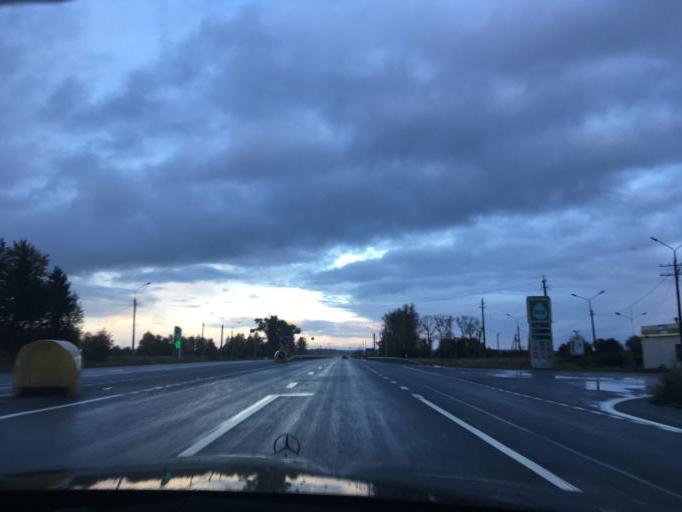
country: RU
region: Smolensk
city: Yartsevo
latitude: 55.0663
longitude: 32.6225
